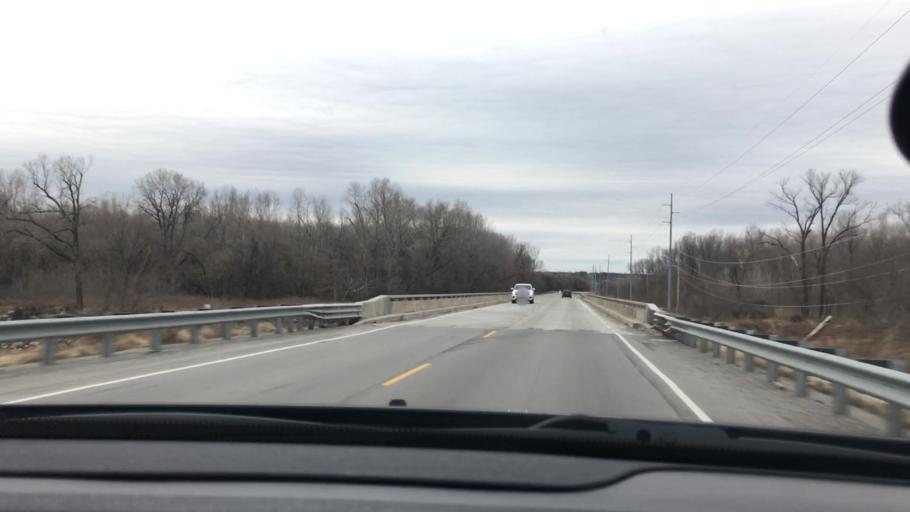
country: US
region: Oklahoma
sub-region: Marshall County
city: Oakland
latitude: 34.2176
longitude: -96.8022
